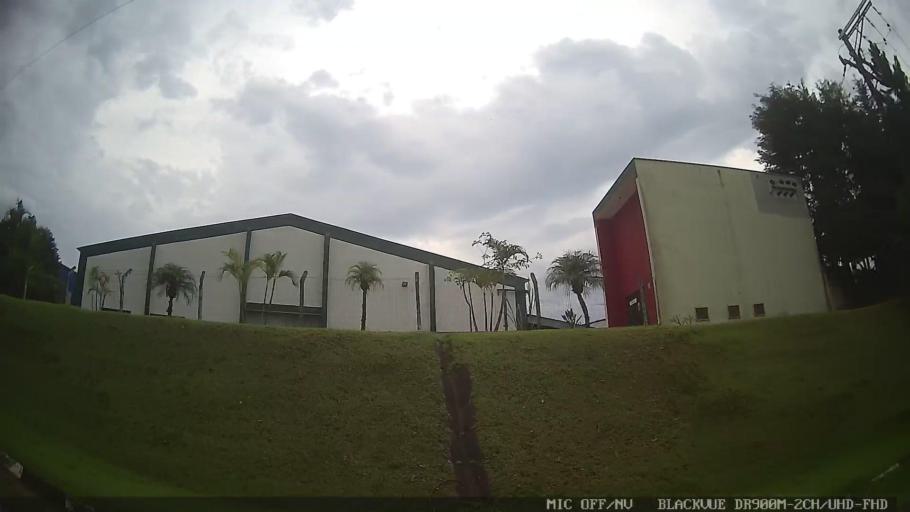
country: BR
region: Sao Paulo
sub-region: Aruja
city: Aruja
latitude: -23.4471
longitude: -46.3095
